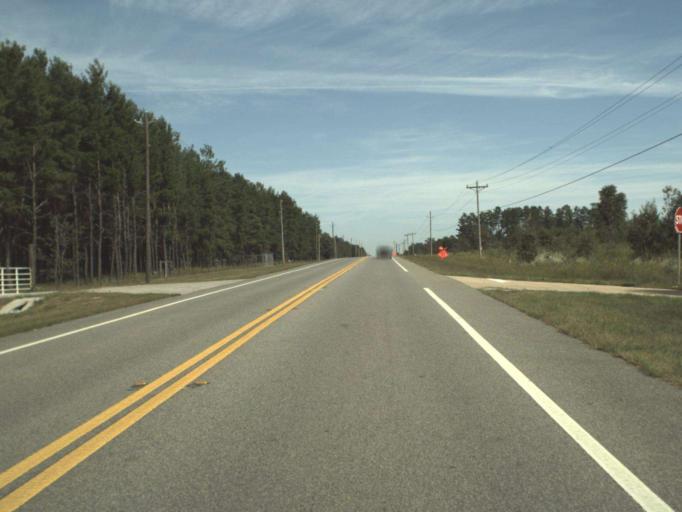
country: US
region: Florida
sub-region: Bay County
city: Youngstown
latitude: 30.5160
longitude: -85.6549
